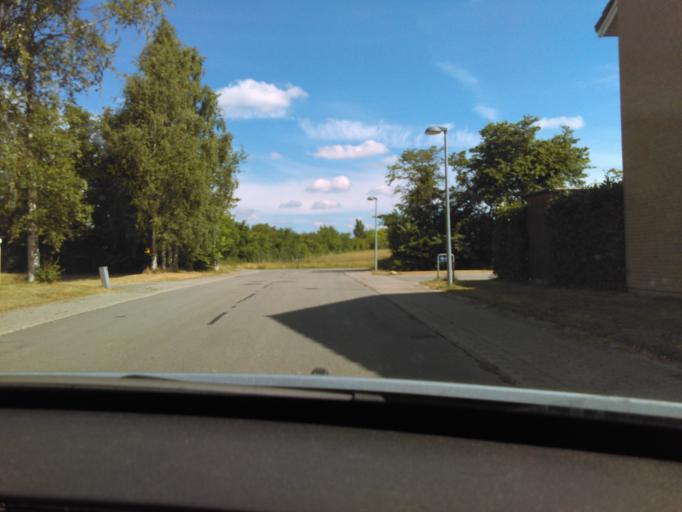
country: DK
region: Capital Region
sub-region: Fureso Kommune
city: Farum
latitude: 55.8254
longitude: 12.3552
